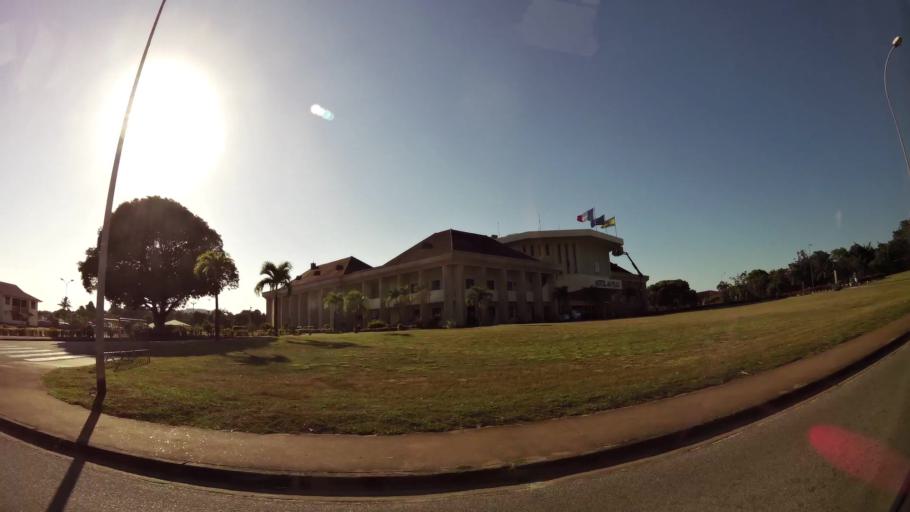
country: GF
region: Guyane
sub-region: Guyane
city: Remire-Montjoly
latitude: 4.9044
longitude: -52.2761
